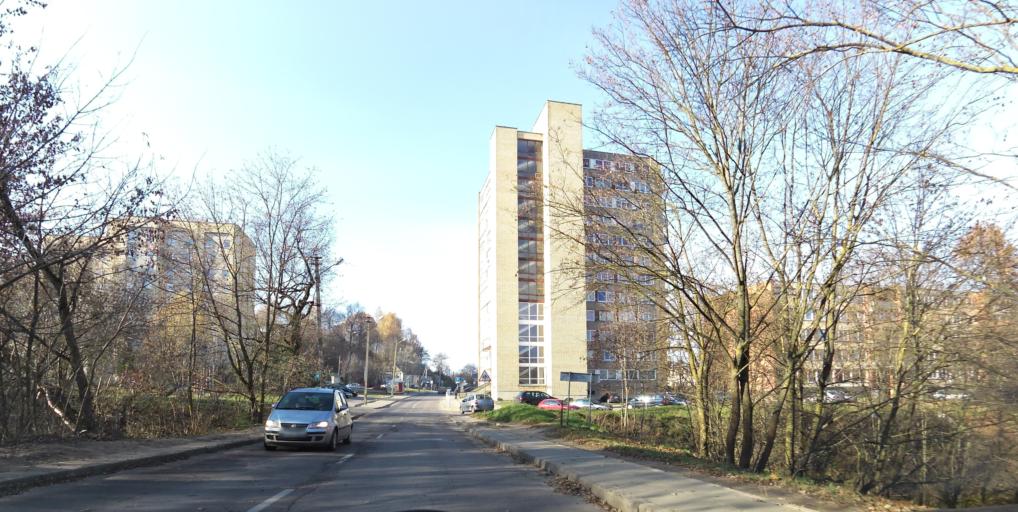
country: LT
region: Vilnius County
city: Rasos
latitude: 54.6744
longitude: 25.3211
